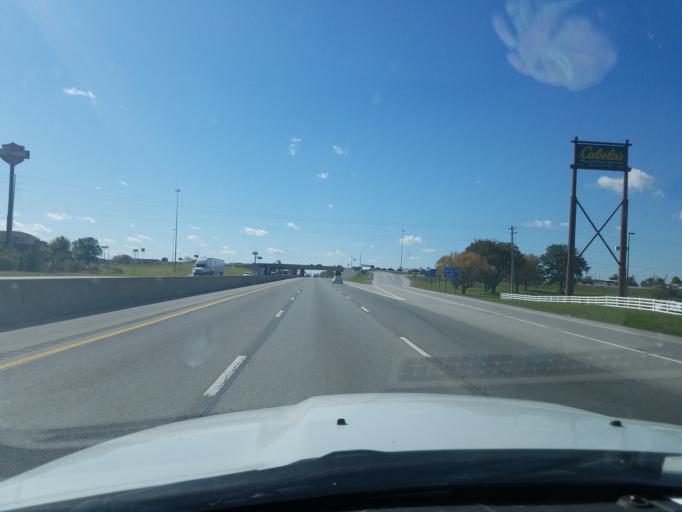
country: US
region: Kentucky
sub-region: Warren County
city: Plano
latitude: 36.9381
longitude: -86.4162
